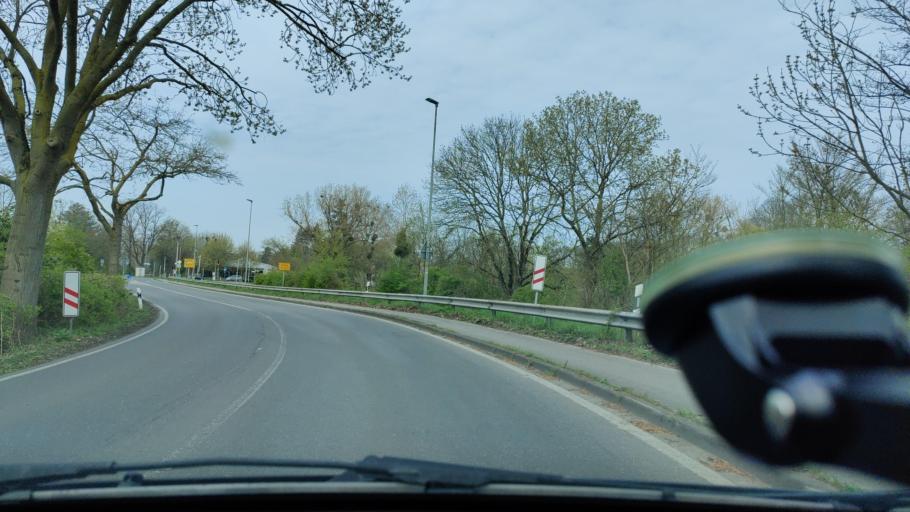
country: DE
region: North Rhine-Westphalia
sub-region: Regierungsbezirk Dusseldorf
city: Dinslaken
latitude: 51.5214
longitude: 6.6810
